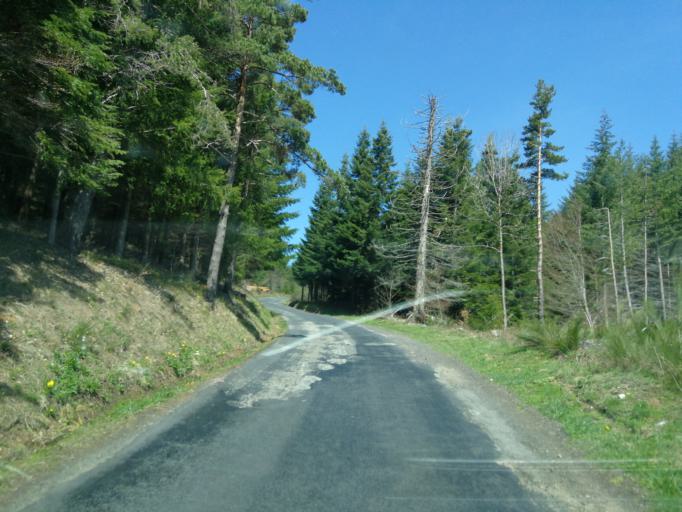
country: FR
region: Rhone-Alpes
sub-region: Departement de l'Ardeche
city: Le Cheylard
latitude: 44.9546
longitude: 4.4182
